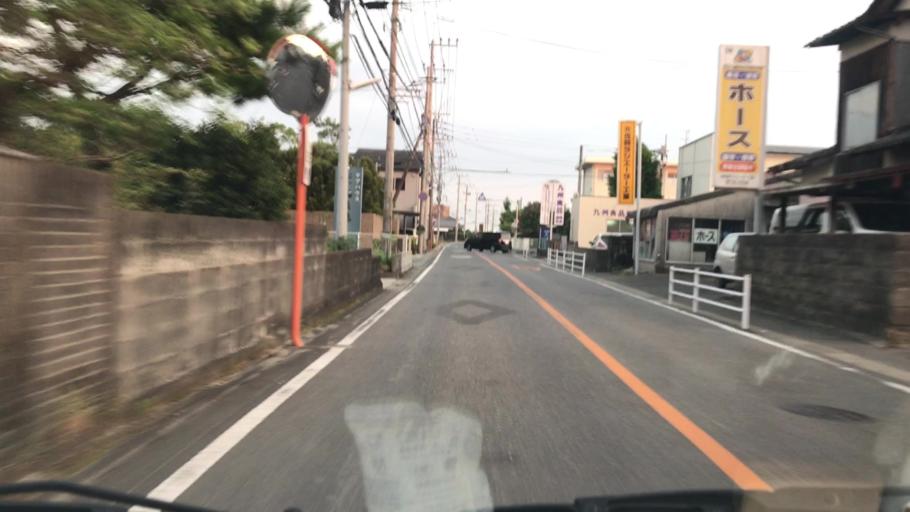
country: JP
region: Saga Prefecture
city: Saga-shi
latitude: 33.2420
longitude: 130.2581
